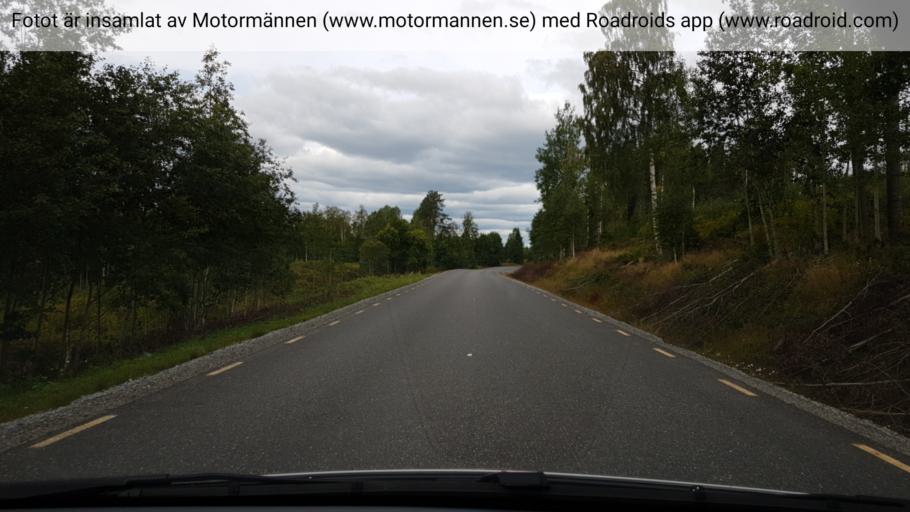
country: SE
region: Vaesterbotten
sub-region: Vannas Kommun
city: Vannasby
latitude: 64.0688
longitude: 19.9353
